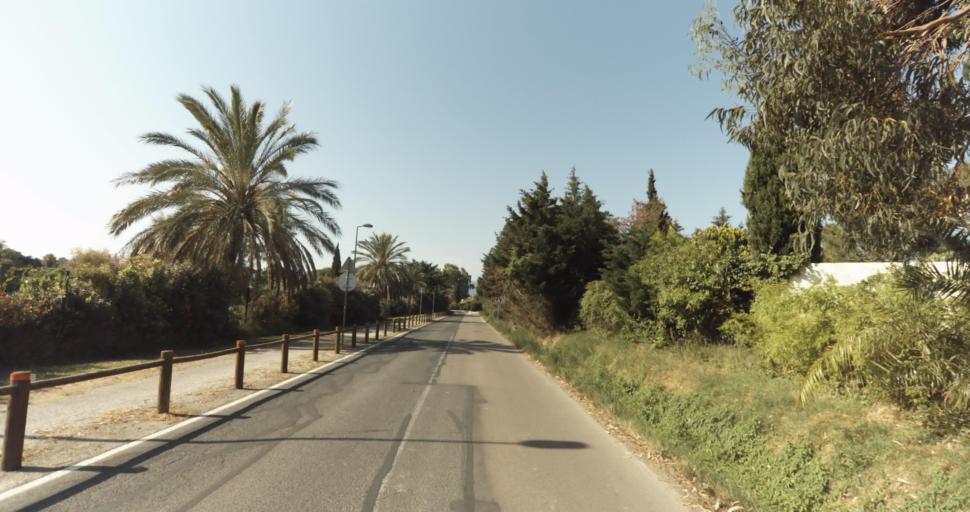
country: FR
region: Languedoc-Roussillon
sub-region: Departement des Pyrenees-Orientales
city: Saint-Cyprien-Plage
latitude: 42.6358
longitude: 3.0126
